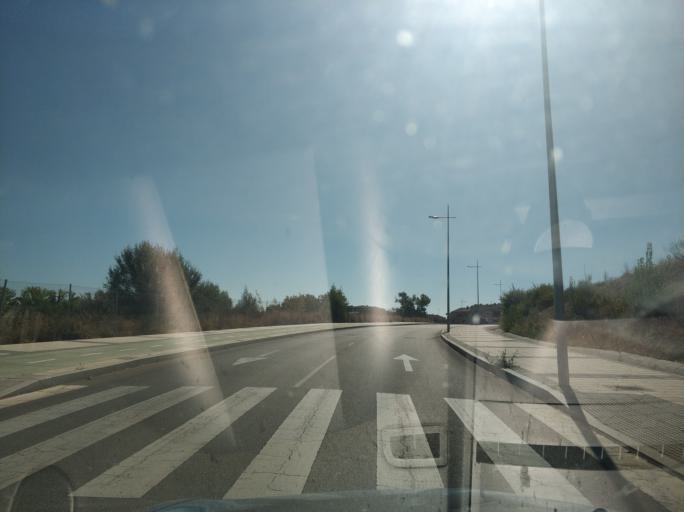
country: ES
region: Castille and Leon
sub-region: Provincia de Burgos
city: Aranda de Duero
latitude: 41.6721
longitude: -3.6948
